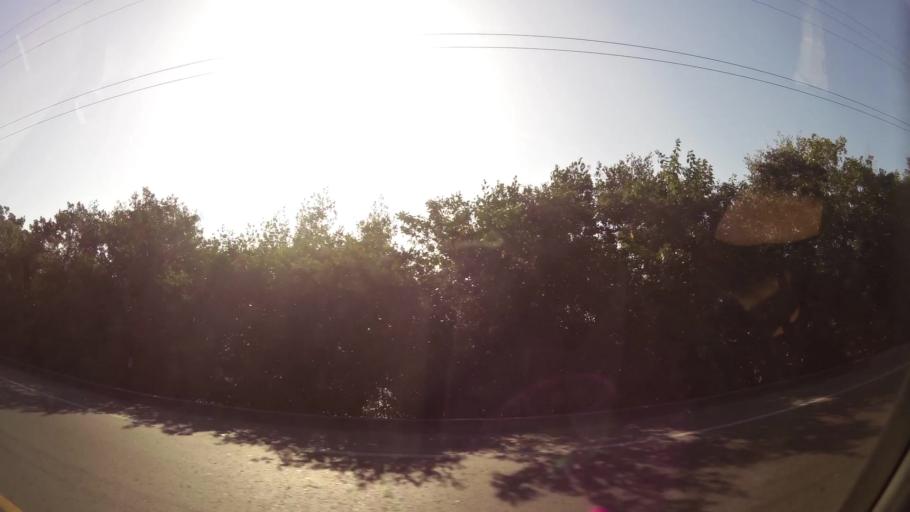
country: CO
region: Bolivar
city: Cartagena
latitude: 10.4759
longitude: -75.4923
